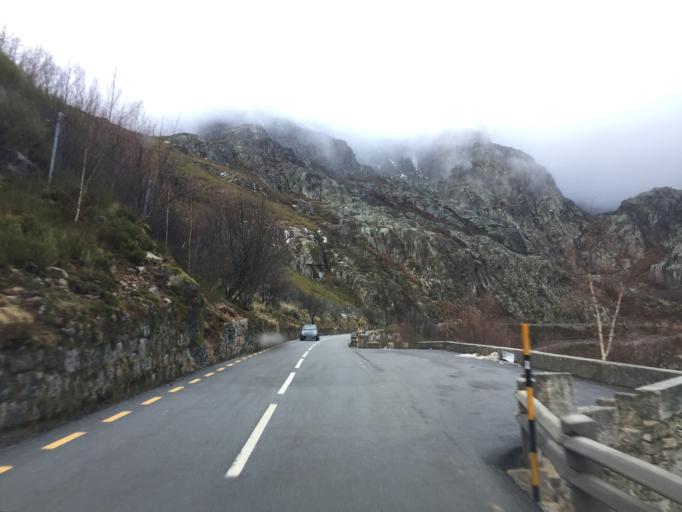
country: PT
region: Castelo Branco
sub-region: Covilha
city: Covilha
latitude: 40.3252
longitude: -7.5812
